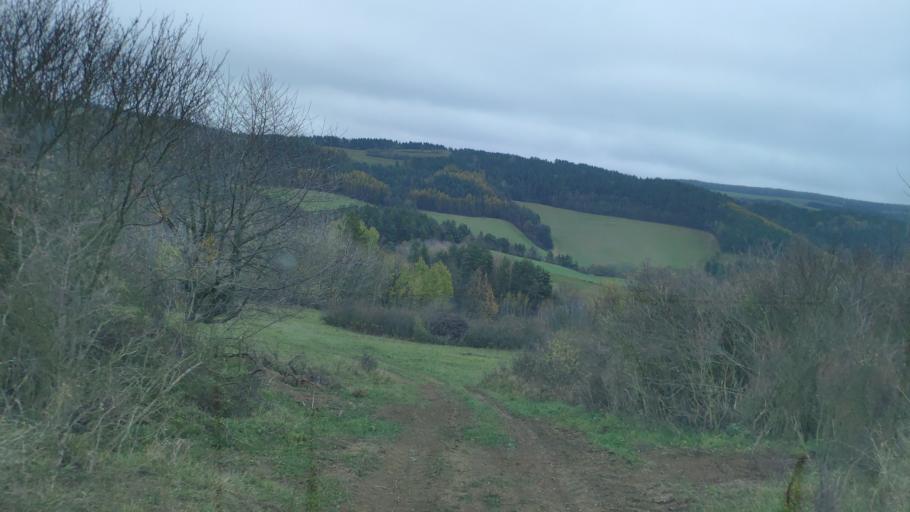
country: SK
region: Presovsky
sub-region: Okres Presov
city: Presov
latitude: 48.9267
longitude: 21.0981
